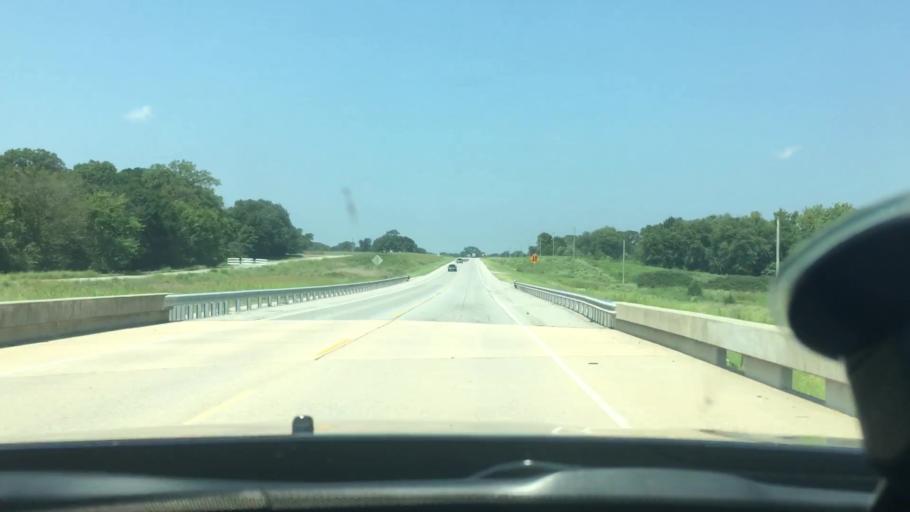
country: US
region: Oklahoma
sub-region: Atoka County
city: Atoka
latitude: 34.2911
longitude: -95.9723
